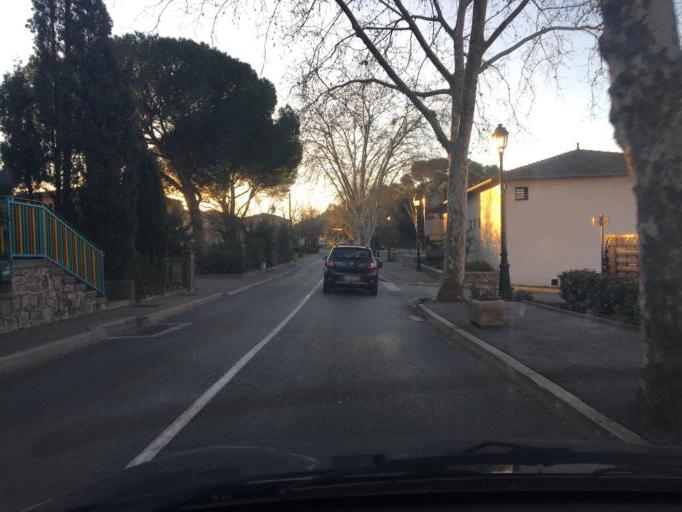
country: FR
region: Provence-Alpes-Cote d'Azur
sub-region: Departement du Var
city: Taradeau
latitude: 43.4534
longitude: 6.4282
